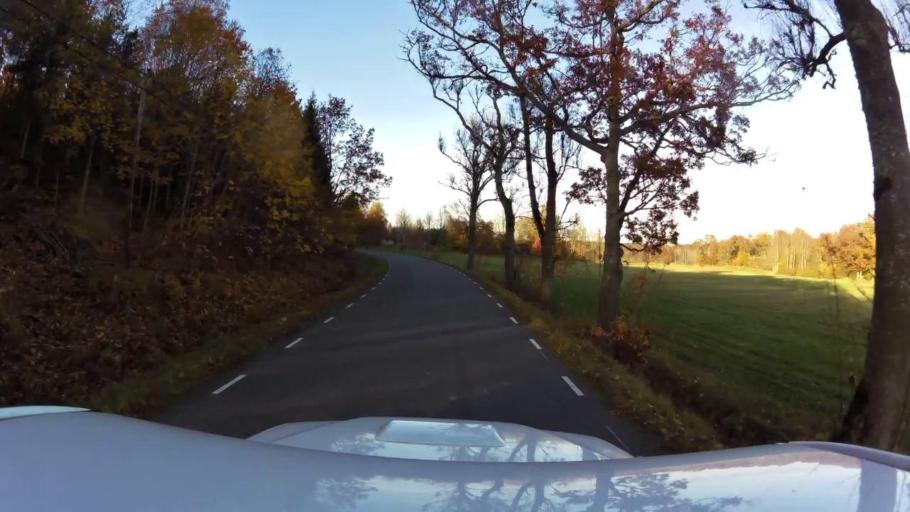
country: SE
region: OEstergoetland
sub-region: Linkopings Kommun
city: Sturefors
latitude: 58.3065
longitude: 15.6670
